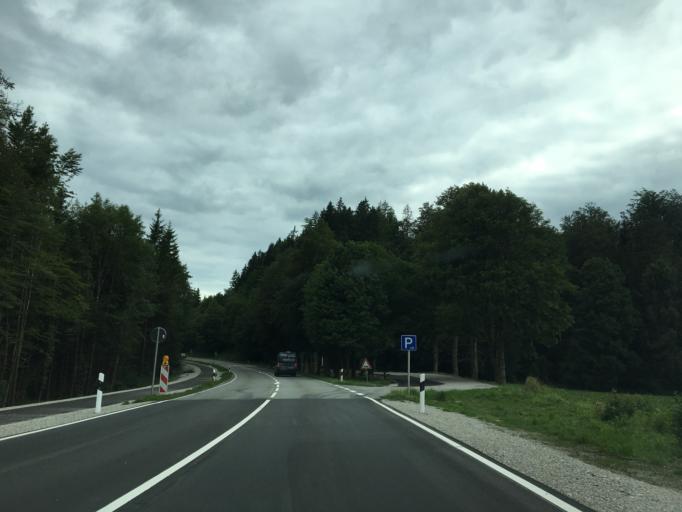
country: DE
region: Bavaria
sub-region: Upper Bavaria
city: Miesbach
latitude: 47.7814
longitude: 11.7842
